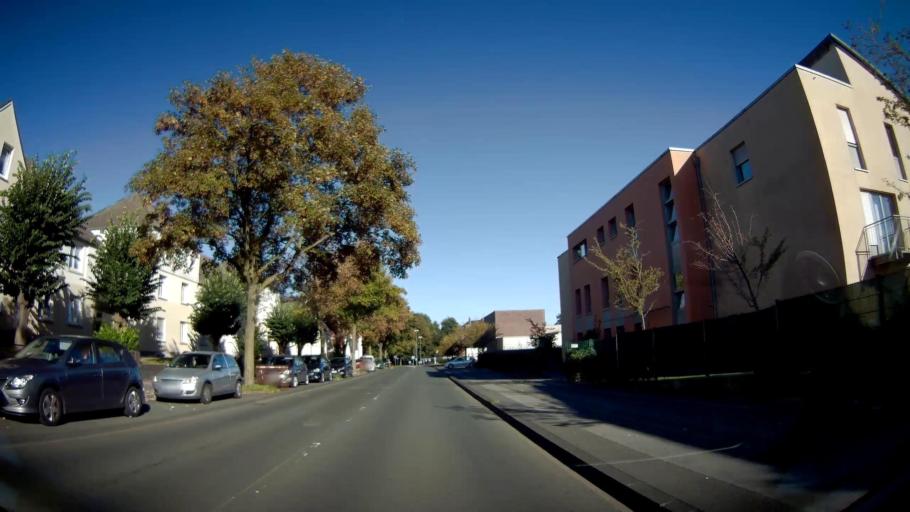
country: DE
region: North Rhine-Westphalia
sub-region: Regierungsbezirk Arnsberg
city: Herne
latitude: 51.5124
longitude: 7.2553
